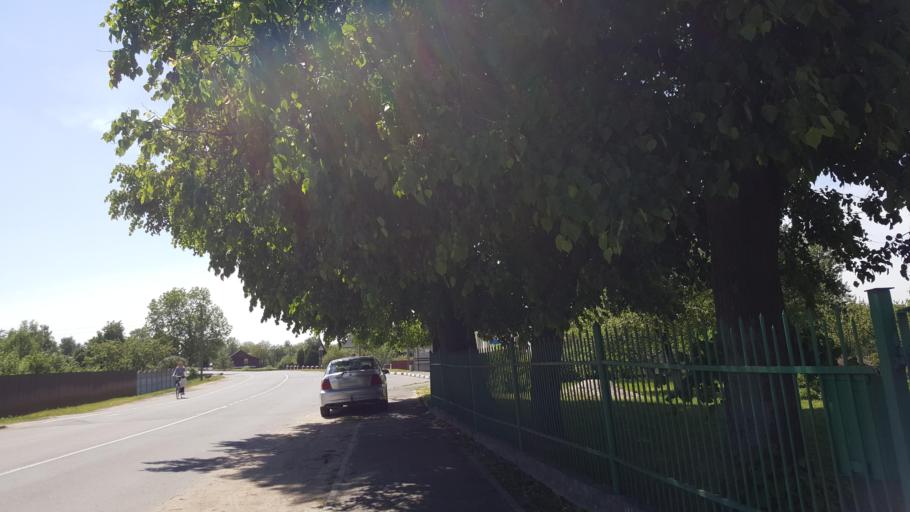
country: BY
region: Brest
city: Charnawchytsy
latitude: 52.2150
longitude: 23.7394
